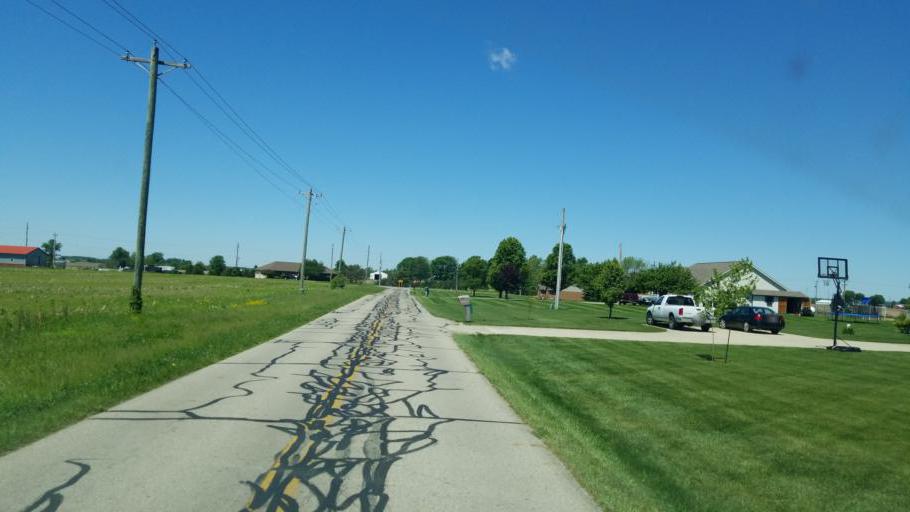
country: US
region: Ohio
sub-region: Shelby County
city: Anna
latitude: 40.3802
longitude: -84.2377
